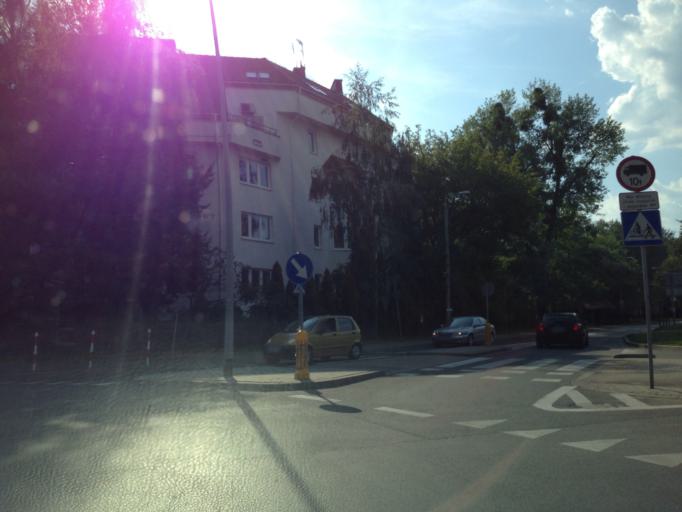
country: PL
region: Masovian Voivodeship
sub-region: Warszawa
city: Bemowo
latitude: 52.2593
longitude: 20.8976
